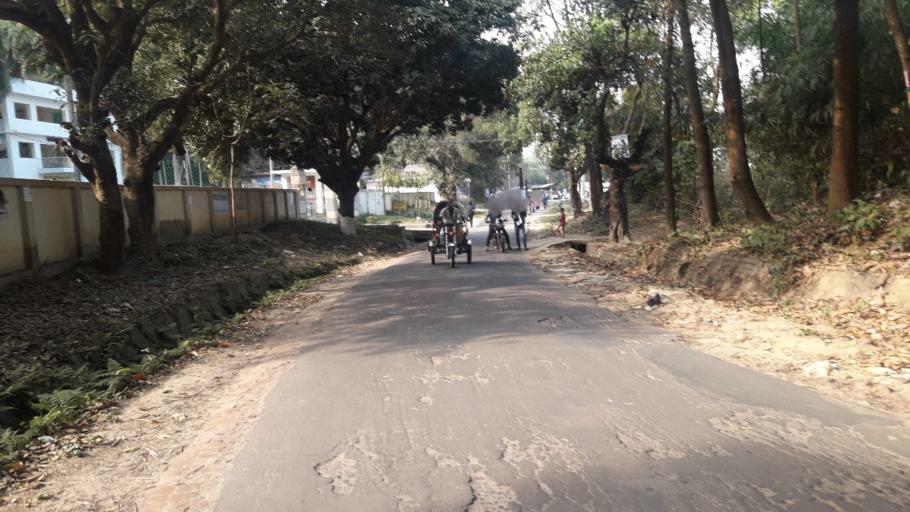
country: BD
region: Chittagong
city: Chittagong
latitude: 22.4698
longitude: 91.7935
